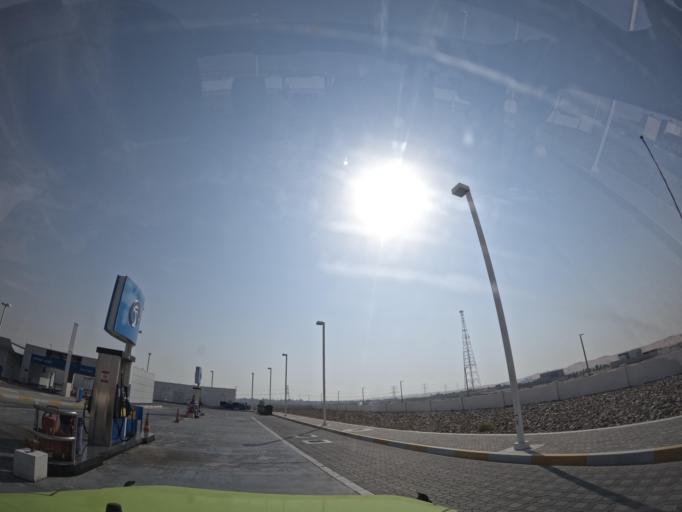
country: OM
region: Al Buraimi
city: Al Buraymi
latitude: 24.5178
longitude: 55.5149
